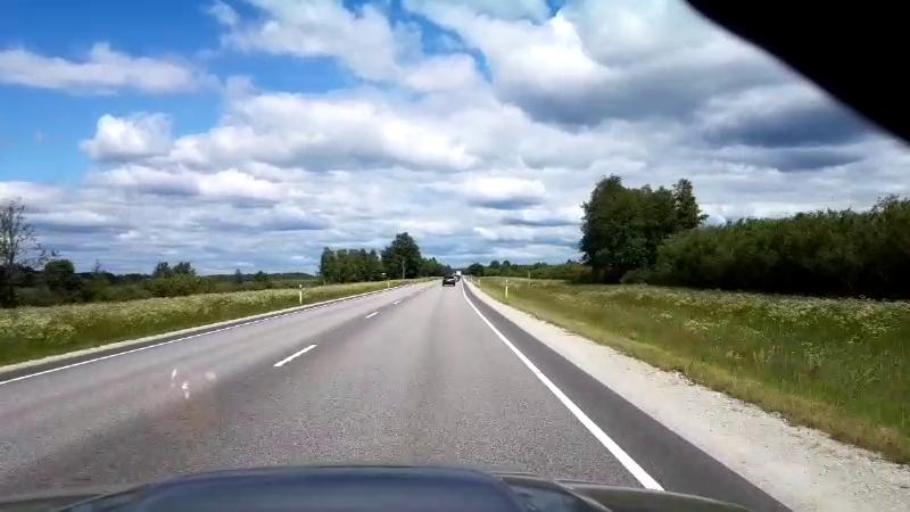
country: EE
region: Paernumaa
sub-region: Sauga vald
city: Sauga
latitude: 58.5000
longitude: 24.5382
